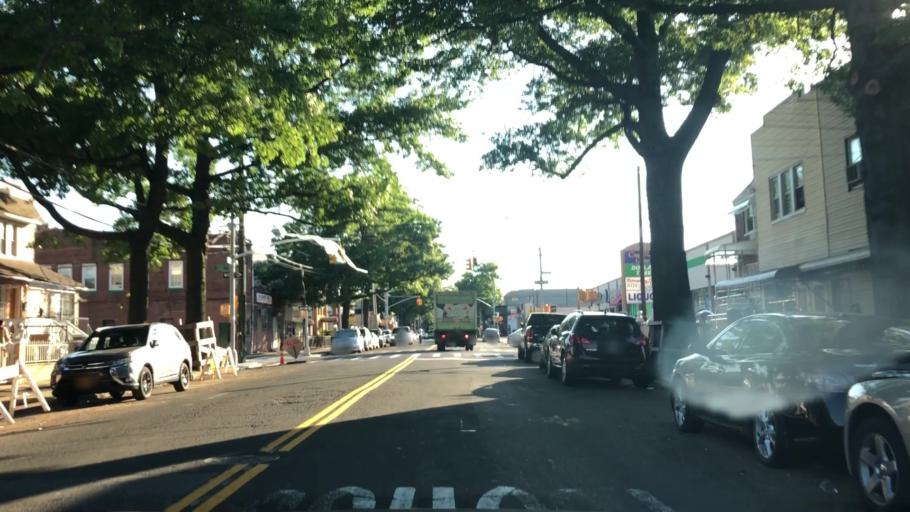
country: US
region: New York
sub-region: Queens County
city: Jamaica
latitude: 40.6932
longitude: -73.8149
